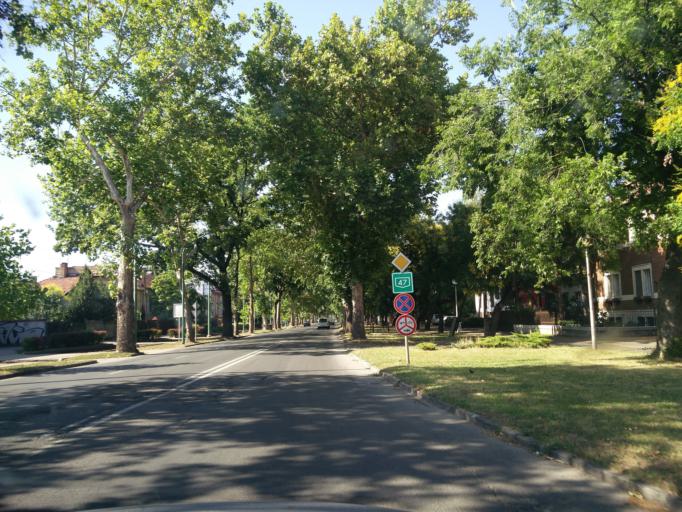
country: HU
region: Csongrad
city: Szeged
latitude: 46.2622
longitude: 20.1578
